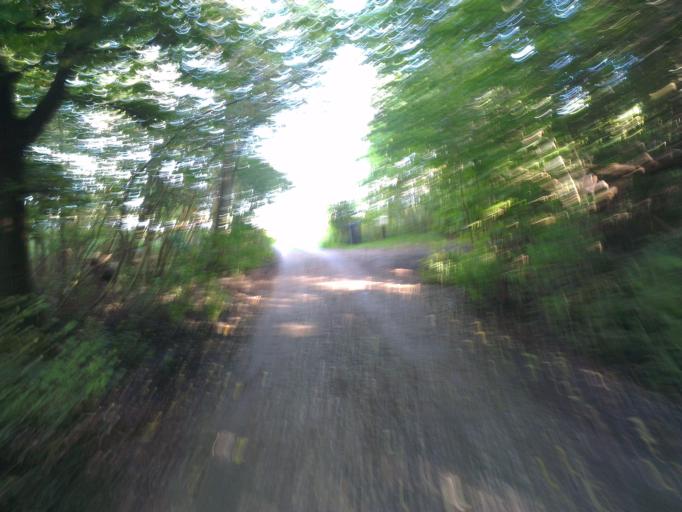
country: DK
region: Capital Region
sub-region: Frederikssund Kommune
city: Frederikssund
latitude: 55.7964
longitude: 12.0543
